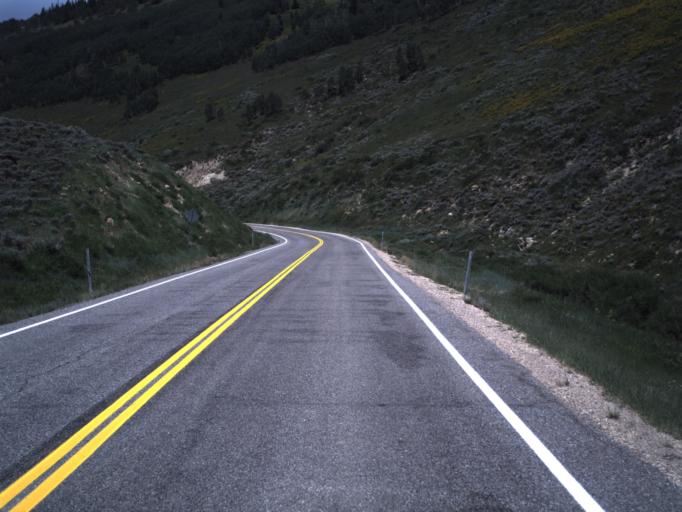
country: US
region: Utah
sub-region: Sanpete County
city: Fairview
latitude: 39.6440
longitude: -111.2466
